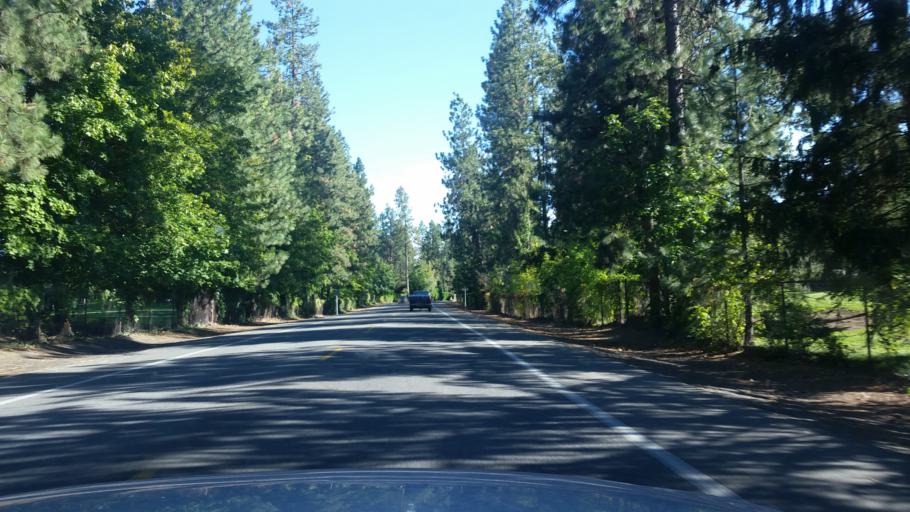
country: US
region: Washington
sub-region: Spokane County
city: Spokane
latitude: 47.6080
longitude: -117.3963
